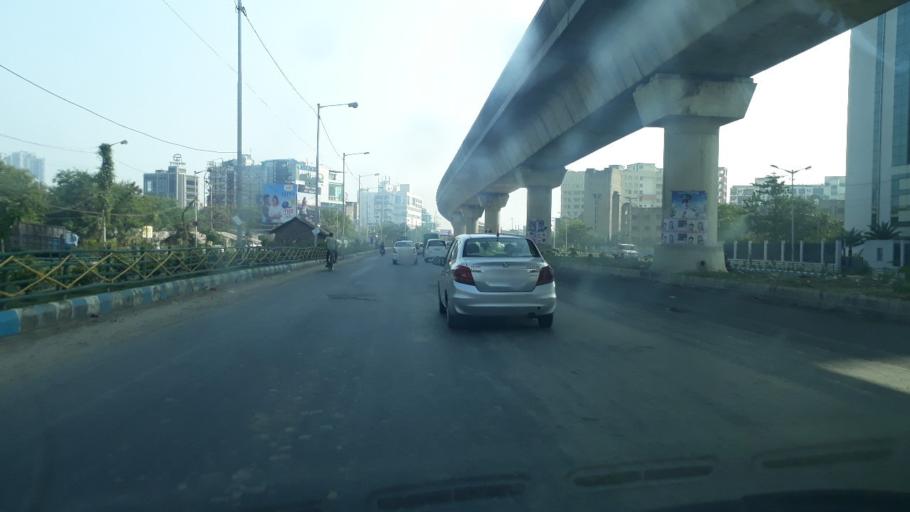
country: IN
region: West Bengal
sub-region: Kolkata
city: Kolkata
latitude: 22.5194
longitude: 88.3996
